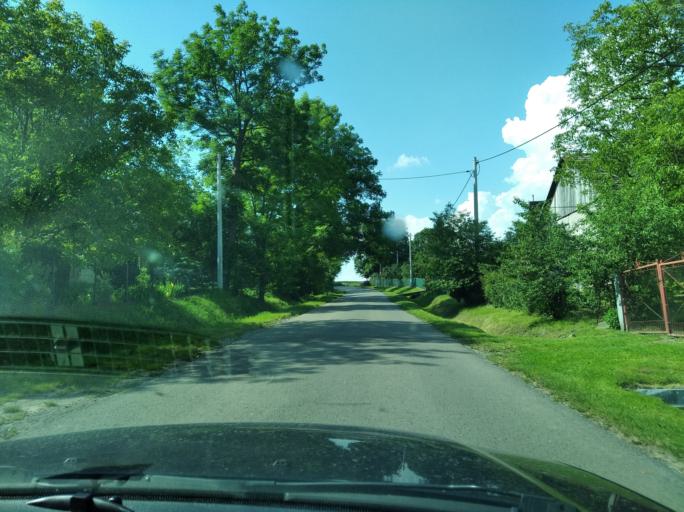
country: PL
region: Subcarpathian Voivodeship
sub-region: Powiat jaroslawski
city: Rokietnica
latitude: 49.9249
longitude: 22.6851
